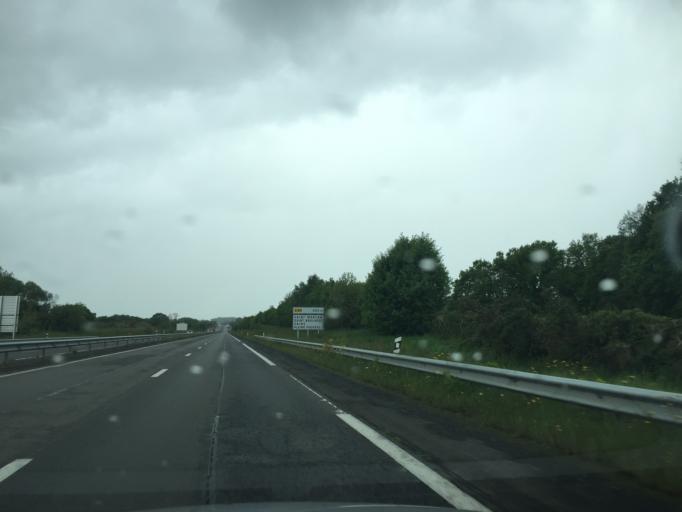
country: FR
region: Brittany
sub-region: Departement d'Ille-et-Vilaine
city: Roz-sur-Couesnon
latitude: 48.5666
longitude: -1.5880
